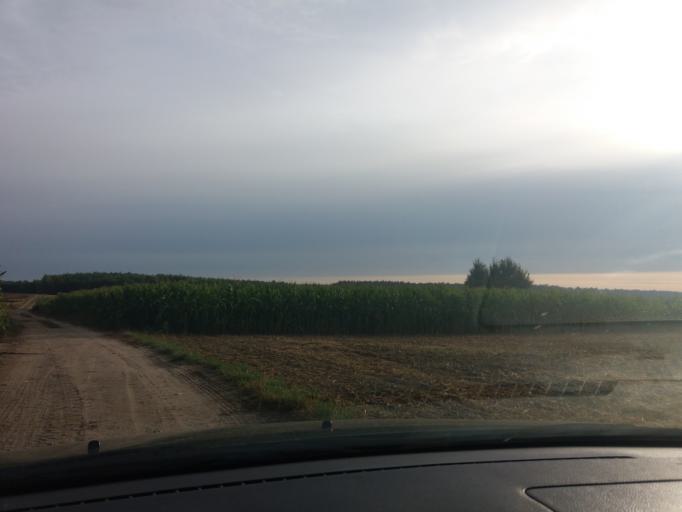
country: PL
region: Masovian Voivodeship
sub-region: Powiat mlawski
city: Wieczfnia Koscielna
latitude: 53.2122
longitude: 20.4546
